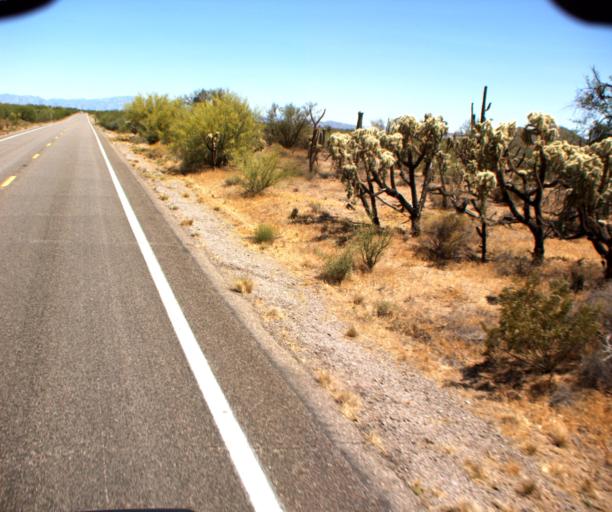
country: US
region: Arizona
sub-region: Pima County
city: Marana
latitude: 32.7564
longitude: -111.1410
